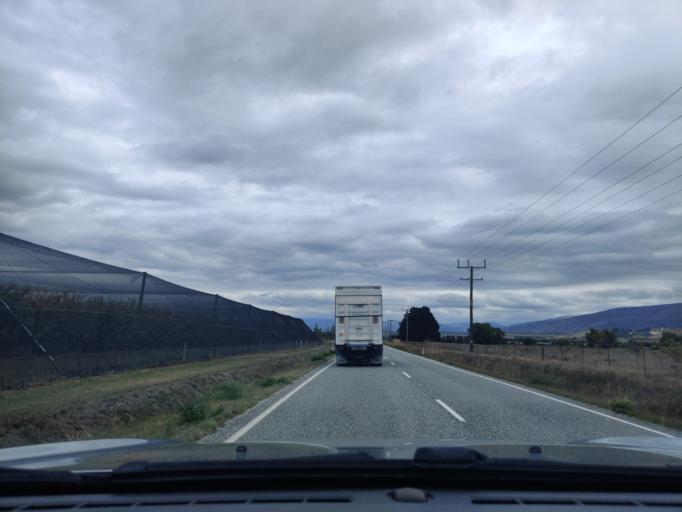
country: NZ
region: Otago
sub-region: Queenstown-Lakes District
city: Wanaka
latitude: -44.9295
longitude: 169.2693
